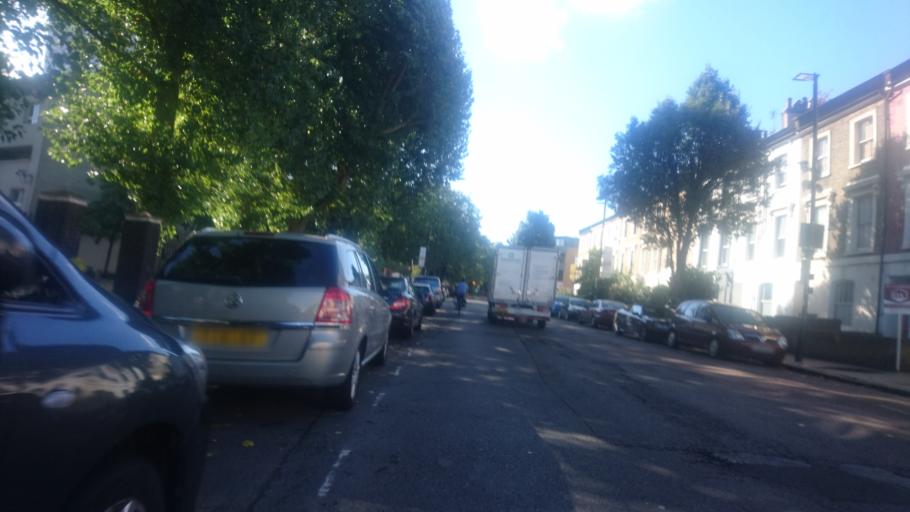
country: GB
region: England
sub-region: Greater London
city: Holloway
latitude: 51.5570
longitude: -0.1122
